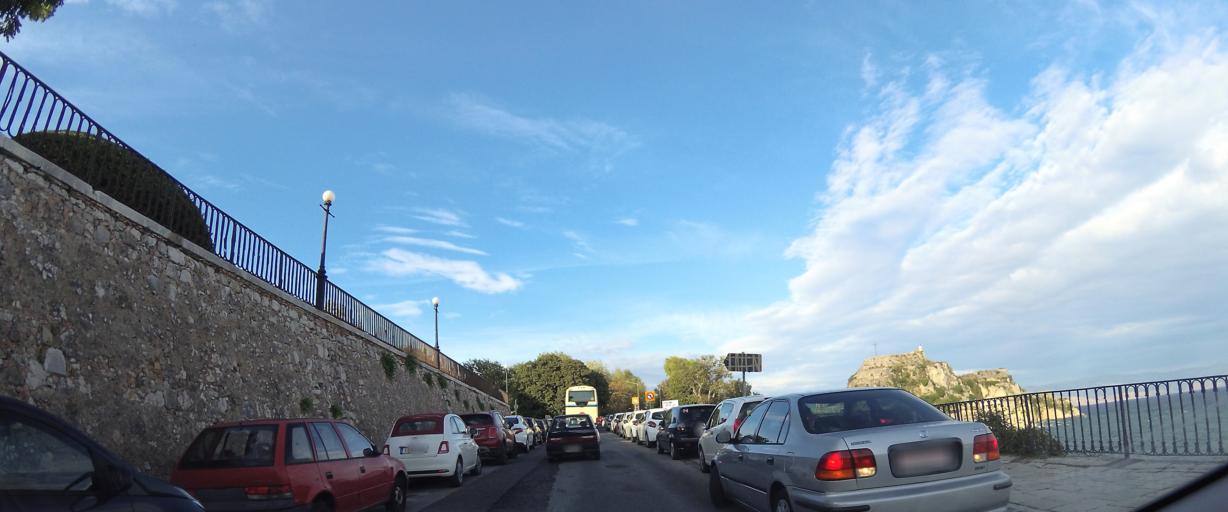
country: GR
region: Ionian Islands
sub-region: Nomos Kerkyras
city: Kerkyra
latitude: 39.6207
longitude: 19.9243
